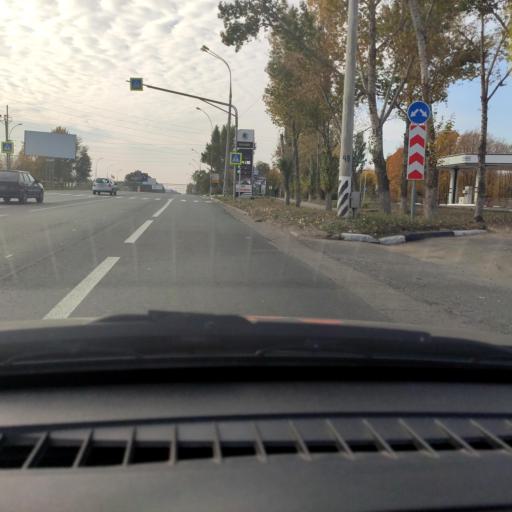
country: RU
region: Samara
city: Tol'yatti
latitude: 53.5467
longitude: 49.2857
